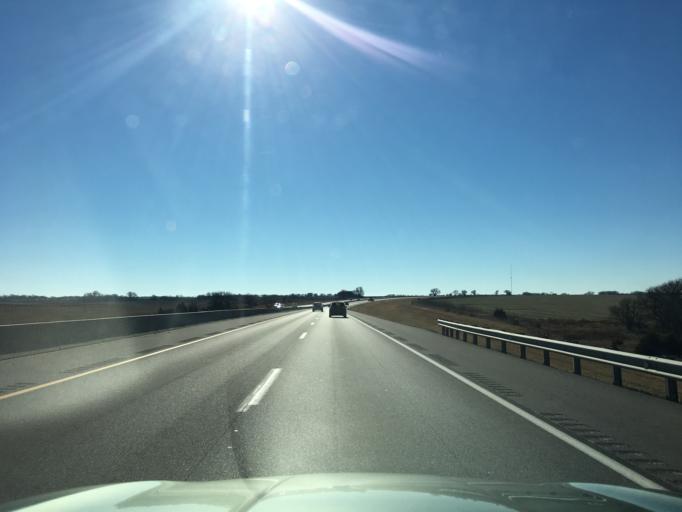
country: US
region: Kansas
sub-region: Sumner County
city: Belle Plaine
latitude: 37.3501
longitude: -97.3221
